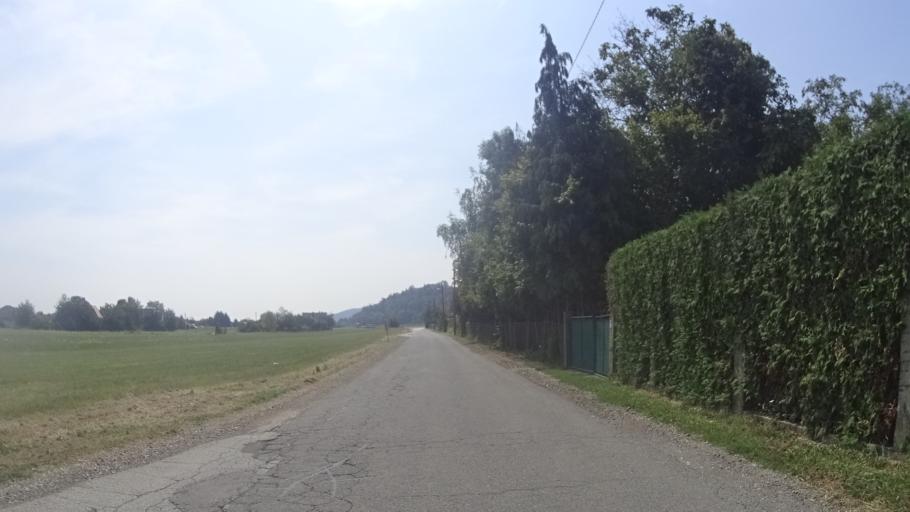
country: SI
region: Maribor
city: Pekre
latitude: 46.5584
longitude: 15.6032
